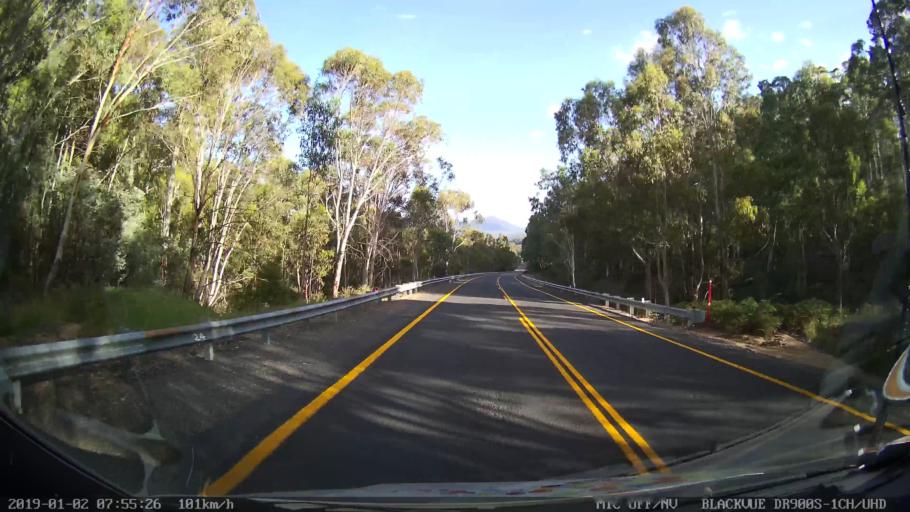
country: AU
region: New South Wales
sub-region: Tumut Shire
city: Tumut
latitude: -35.6849
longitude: 148.4870
